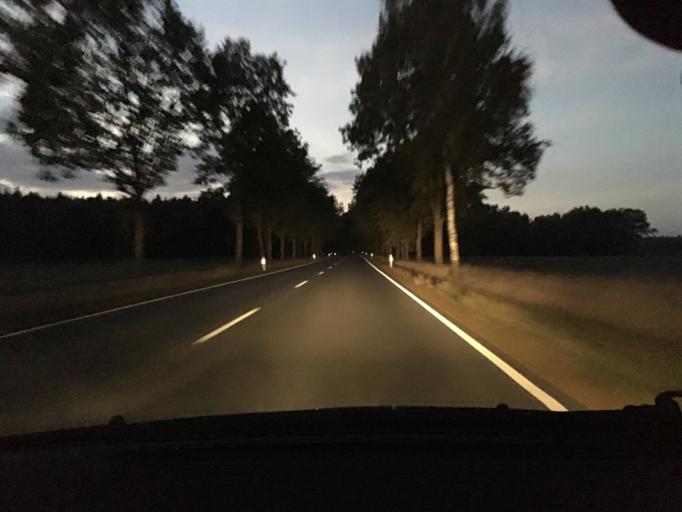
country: DE
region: Lower Saxony
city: Schnega
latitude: 52.9165
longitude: 10.8869
